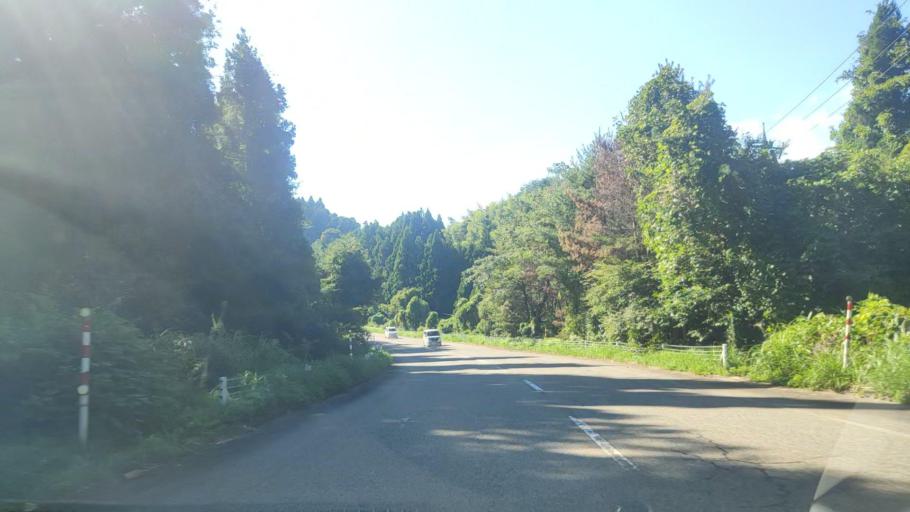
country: JP
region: Ishikawa
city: Nanao
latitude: 37.3151
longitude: 137.1527
